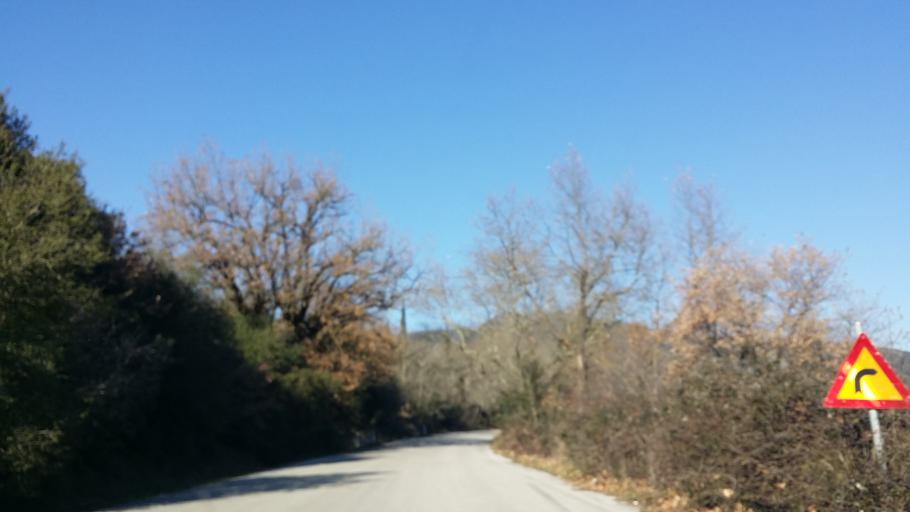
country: GR
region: West Greece
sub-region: Nomos Aitolias kai Akarnanias
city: Sardinia
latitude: 38.8619
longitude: 21.3385
